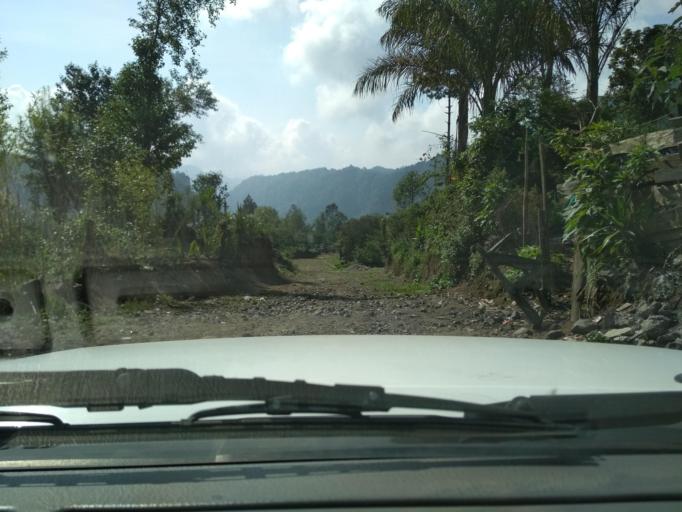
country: MX
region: Veracruz
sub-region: La Perla
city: Chilapa
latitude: 18.9890
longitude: -97.1798
